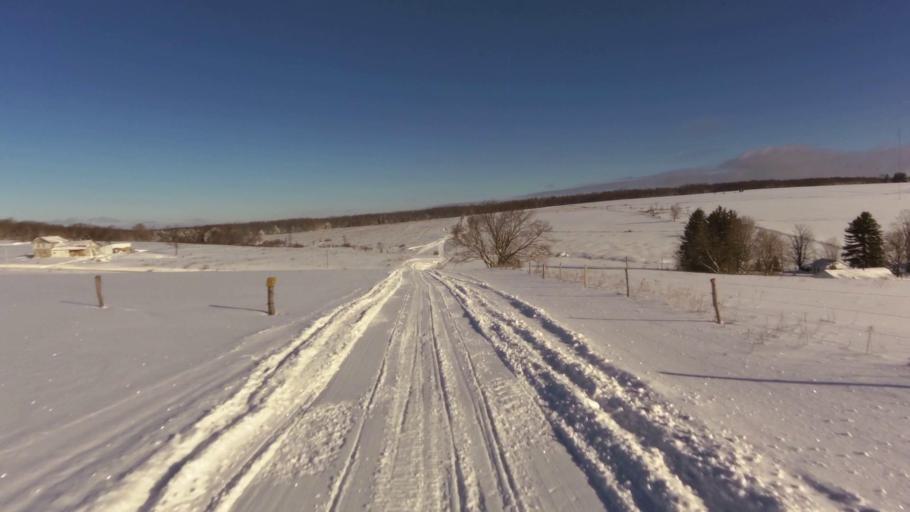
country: US
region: New York
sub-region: Chautauqua County
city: Falconer
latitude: 42.2596
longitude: -79.2029
